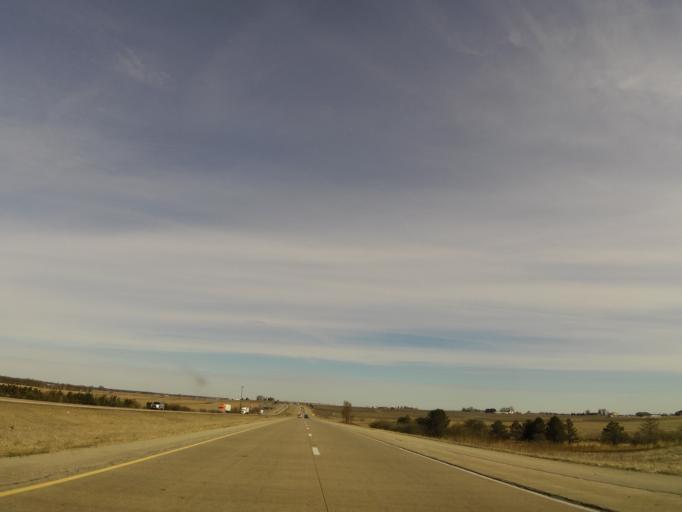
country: US
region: Illinois
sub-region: LaSalle County
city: La Salle
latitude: 41.3695
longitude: -89.0590
